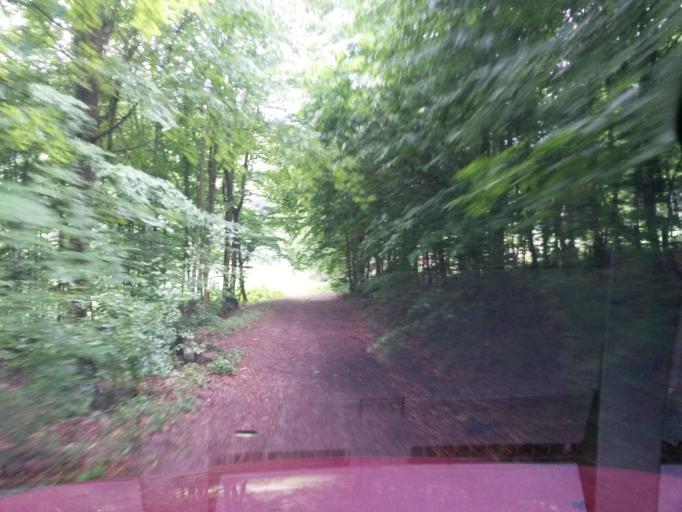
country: SK
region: Kosicky
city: Kosice
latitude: 48.7220
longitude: 21.1686
